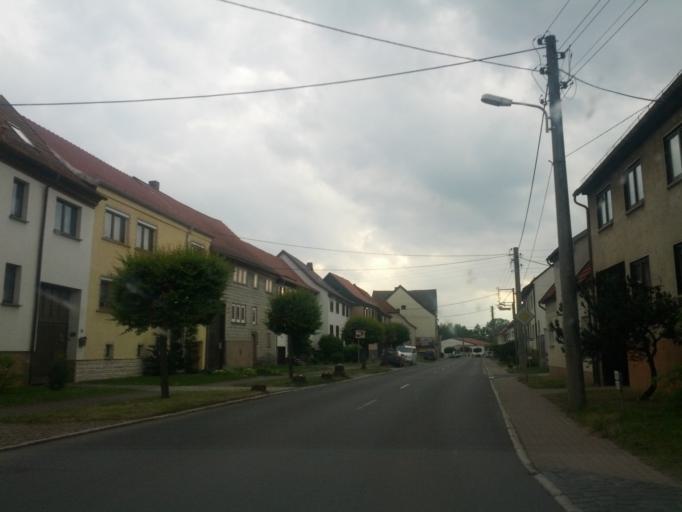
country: DE
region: Thuringia
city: Emleben
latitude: 50.8931
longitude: 10.6978
